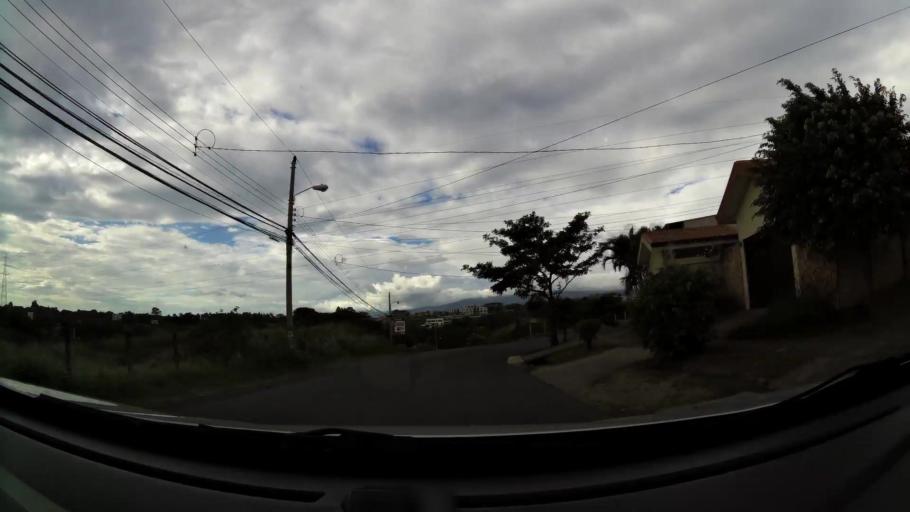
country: CR
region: Heredia
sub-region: Canton de Belen
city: San Antonio
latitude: 9.9654
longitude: -84.1959
